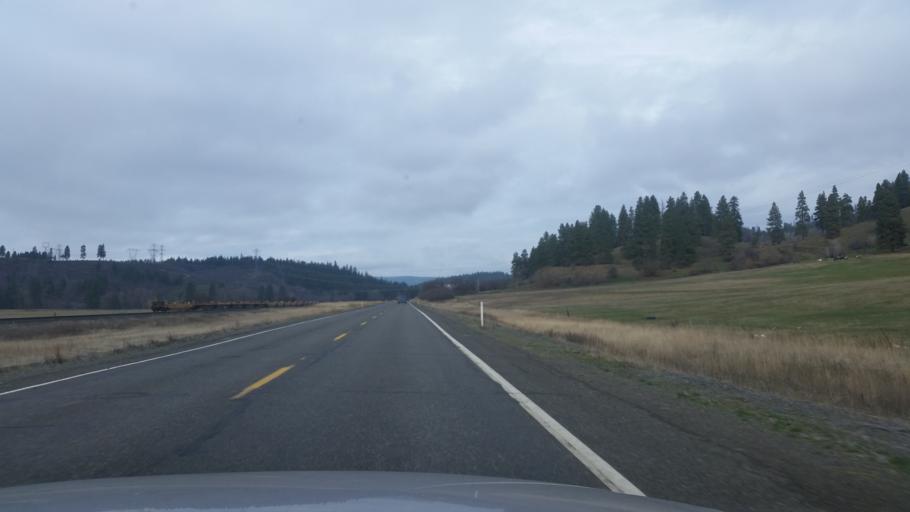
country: US
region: Washington
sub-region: Kittitas County
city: Cle Elum
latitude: 47.1460
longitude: -120.7990
